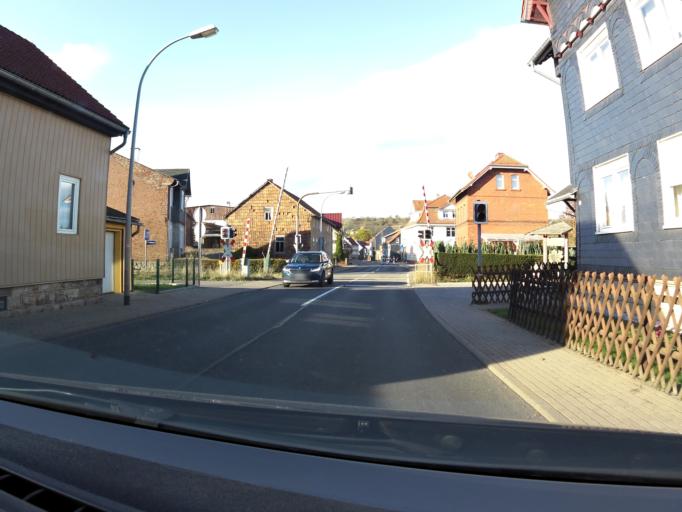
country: DE
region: Thuringia
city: Grafenroda
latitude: 50.7458
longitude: 10.8139
